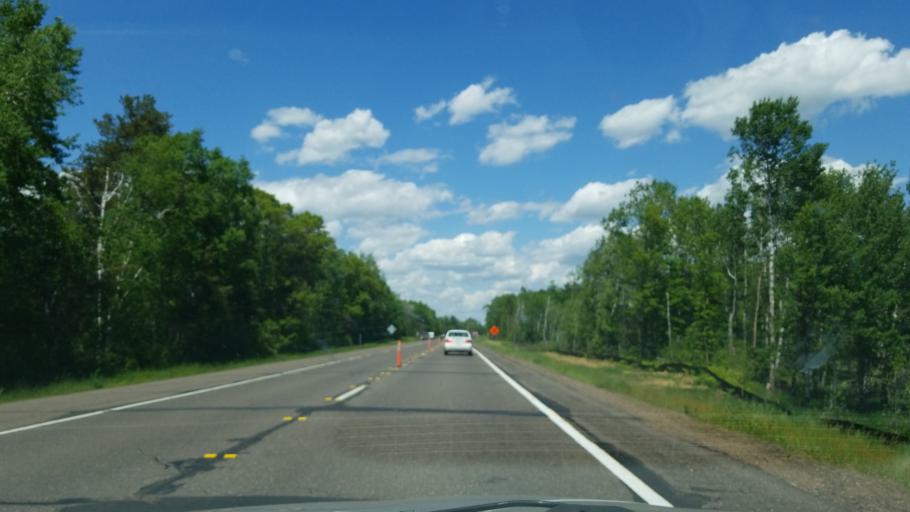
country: US
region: Minnesota
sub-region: Carlton County
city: Moose Lake
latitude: 46.3880
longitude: -92.7813
